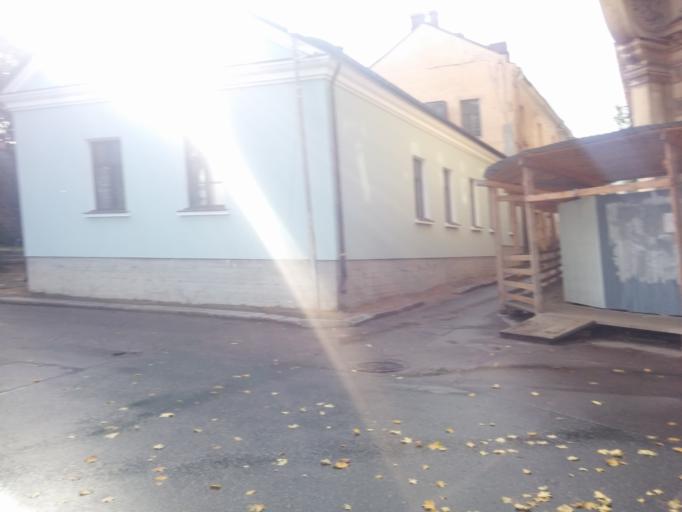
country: RU
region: Leningrad
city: Vyborg
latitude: 60.7147
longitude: 28.7347
